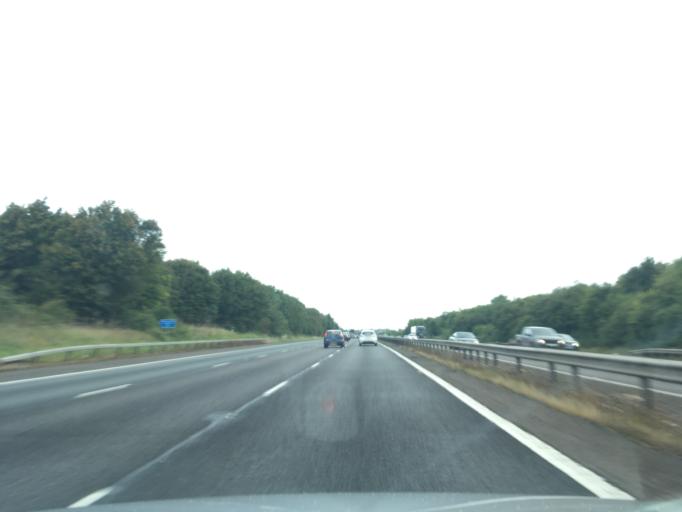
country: GB
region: England
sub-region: Oxfordshire
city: Bicester
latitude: 51.8967
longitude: -1.2064
